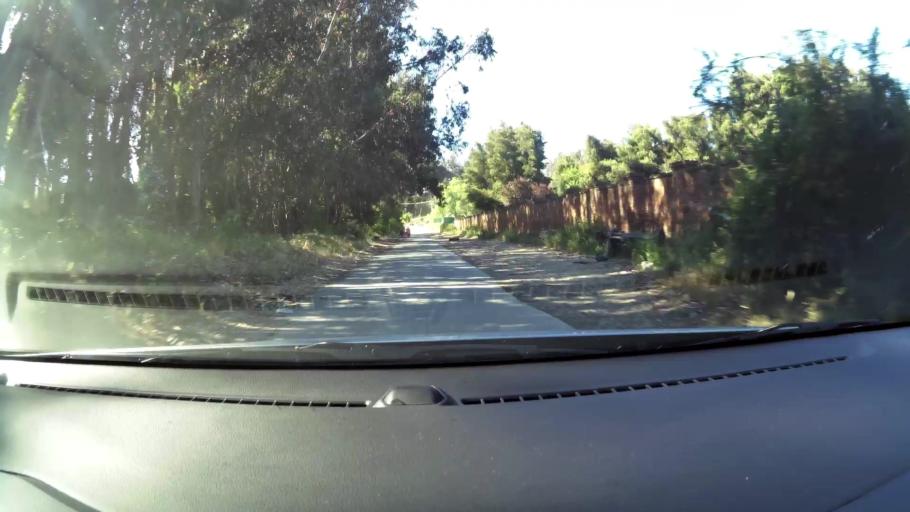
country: CL
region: Valparaiso
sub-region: Provincia de Valparaiso
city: Vina del Mar
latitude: -33.1442
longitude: -71.5607
